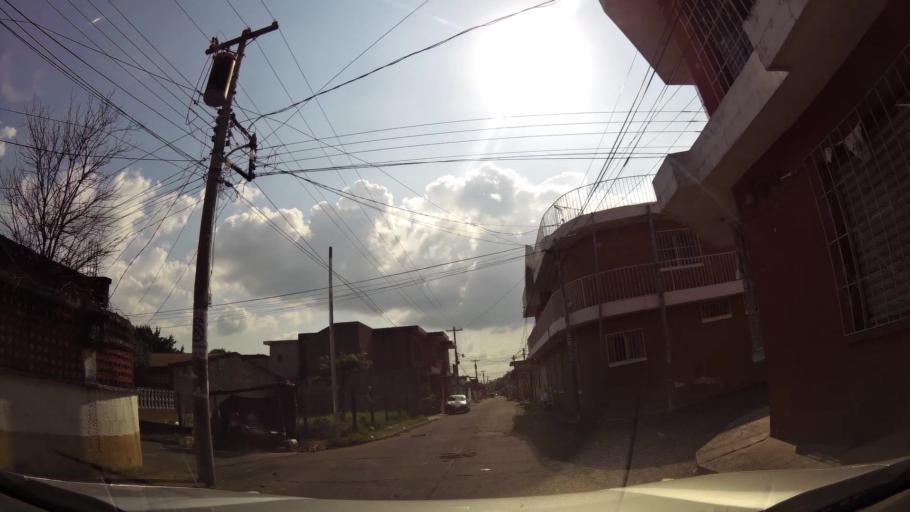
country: GT
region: Retalhuleu
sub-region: Municipio de Retalhuleu
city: Retalhuleu
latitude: 14.5405
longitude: -91.6841
